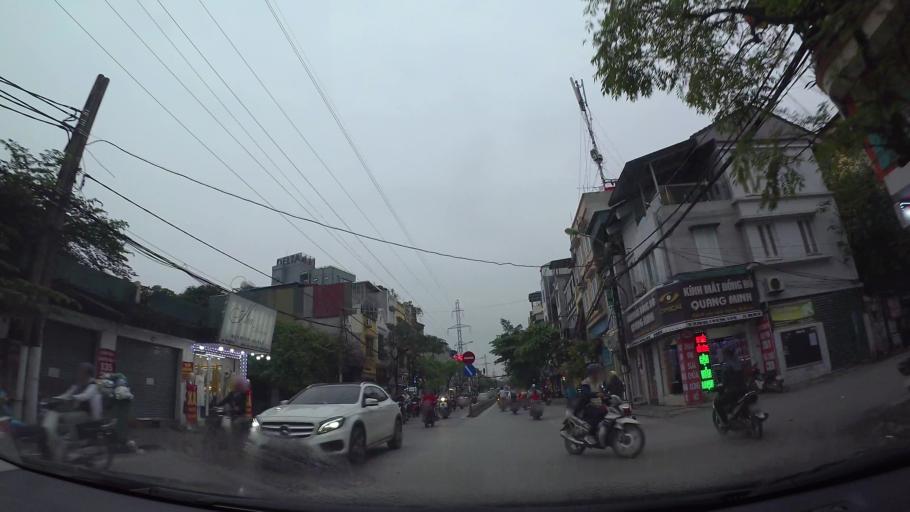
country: VN
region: Ha Noi
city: Hai BaTrung
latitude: 21.0023
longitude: 105.8701
